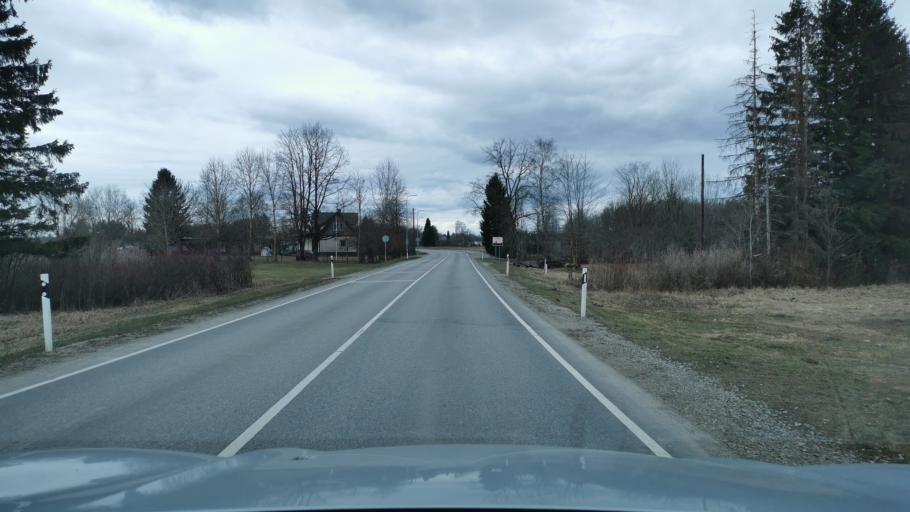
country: EE
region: Ida-Virumaa
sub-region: Puessi linn
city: Pussi
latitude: 59.3567
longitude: 27.0228
